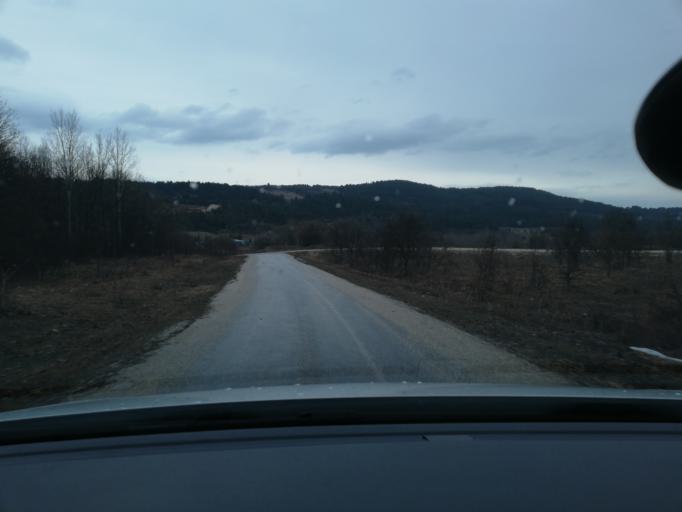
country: TR
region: Bolu
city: Yenicaga
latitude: 40.7546
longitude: 31.9319
